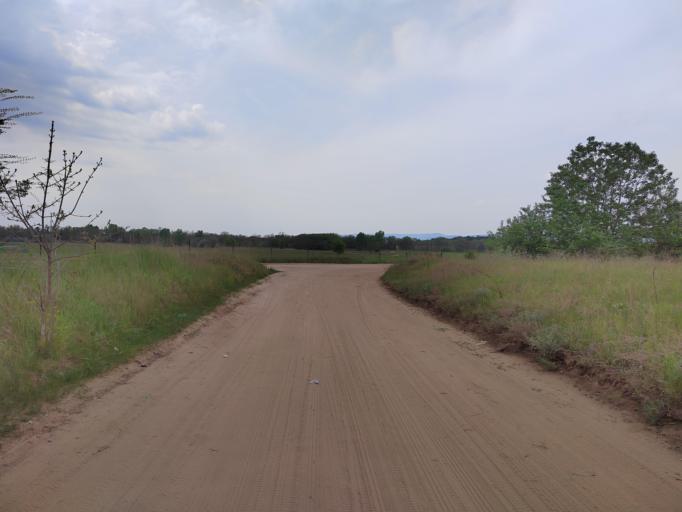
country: HU
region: Pest
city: Fot
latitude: 47.5894
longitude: 19.1903
